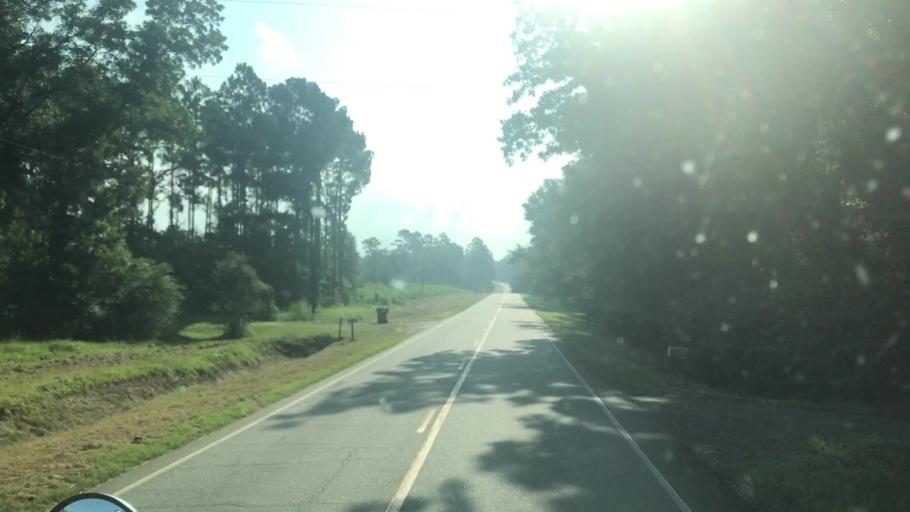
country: US
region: Florida
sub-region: Gadsden County
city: Quincy
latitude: 30.6992
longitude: -84.5291
